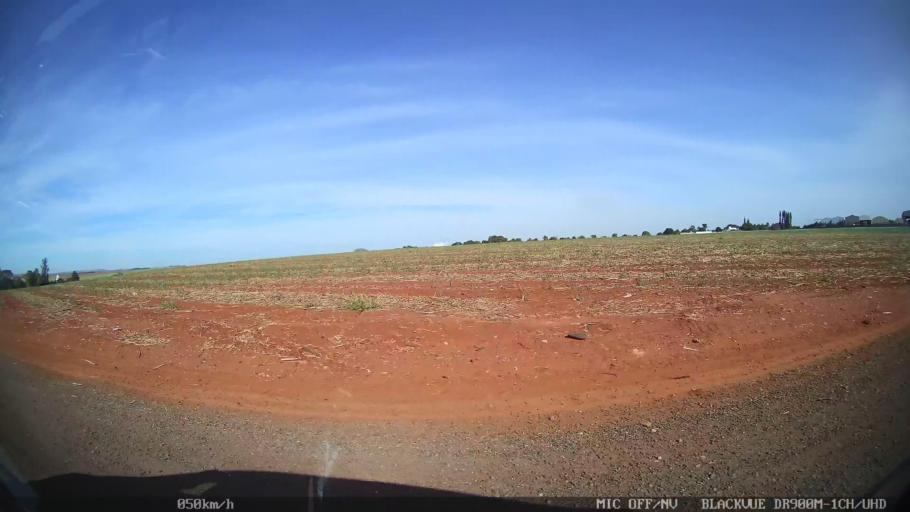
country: BR
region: Sao Paulo
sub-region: Piracicaba
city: Piracicaba
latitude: -22.7870
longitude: -47.6482
